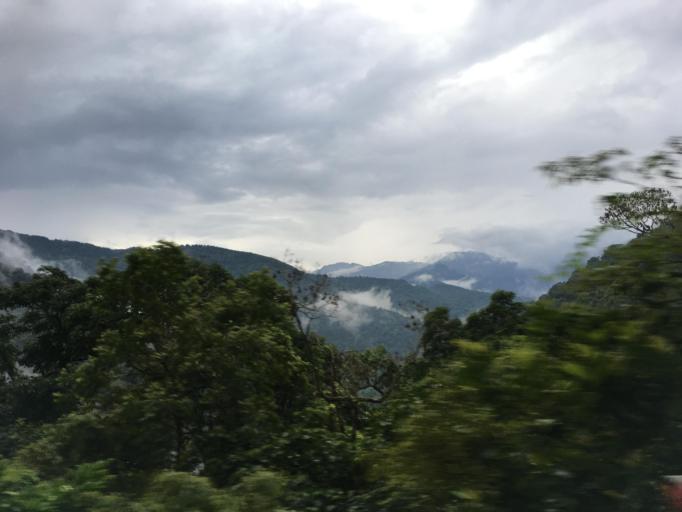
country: TW
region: Taiwan
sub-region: Yilan
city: Yilan
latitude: 24.5528
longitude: 121.5100
